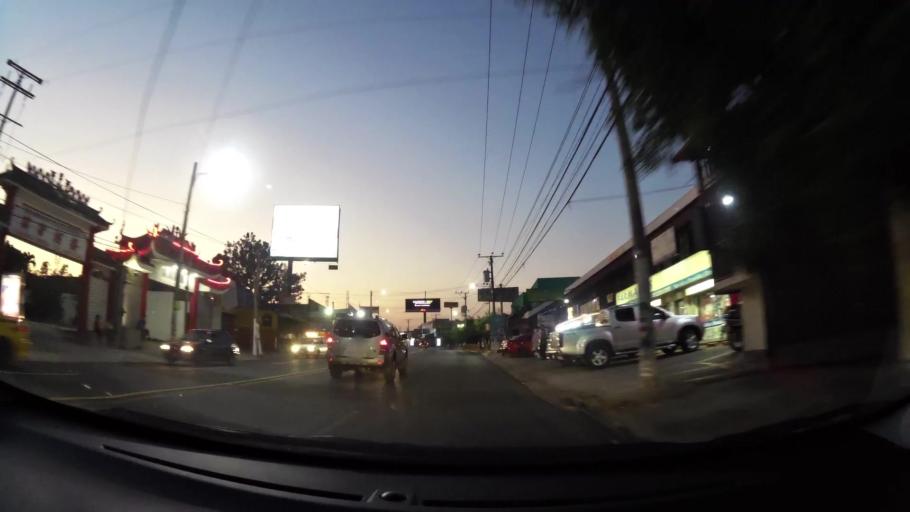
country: SV
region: La Libertad
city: Santa Tecla
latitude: 13.6793
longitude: -89.2702
